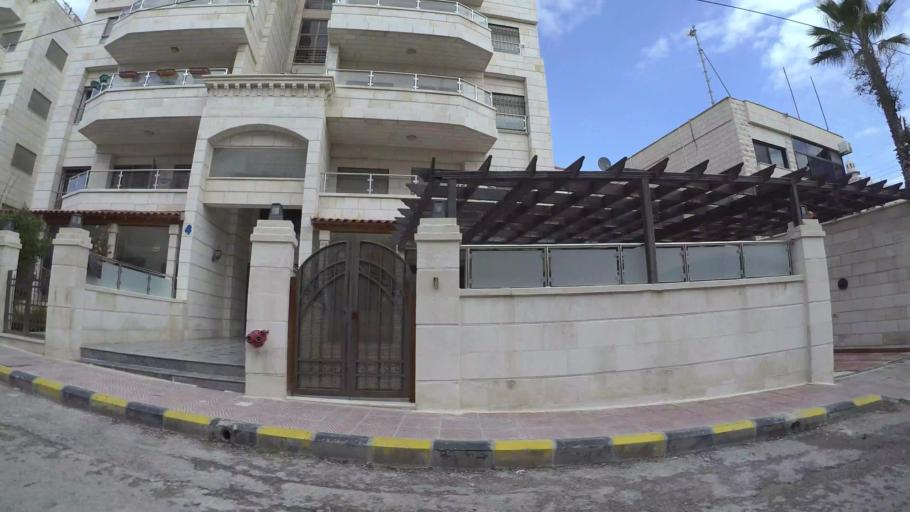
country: JO
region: Amman
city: Al Jubayhah
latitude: 31.9824
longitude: 35.8975
